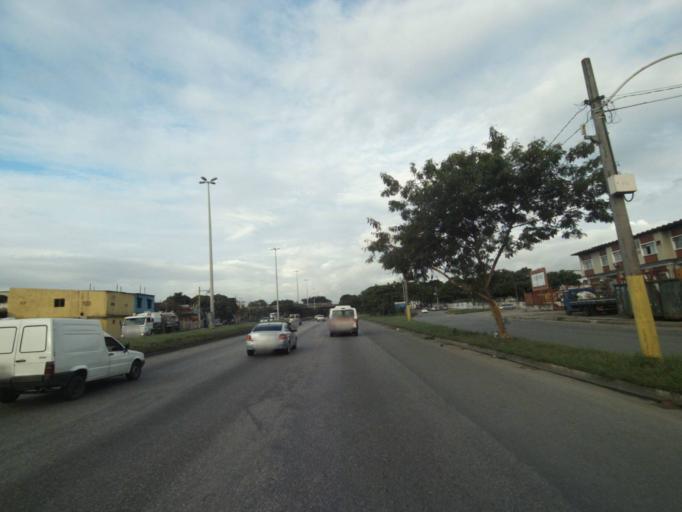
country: BR
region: Rio de Janeiro
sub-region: Nilopolis
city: Nilopolis
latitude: -22.8619
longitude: -43.4467
